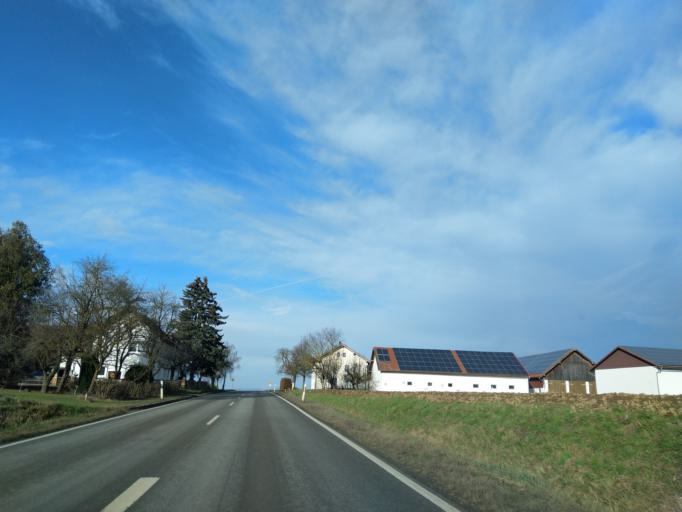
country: DE
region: Bavaria
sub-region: Lower Bavaria
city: Osterhofen
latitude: 48.6660
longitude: 13.0387
